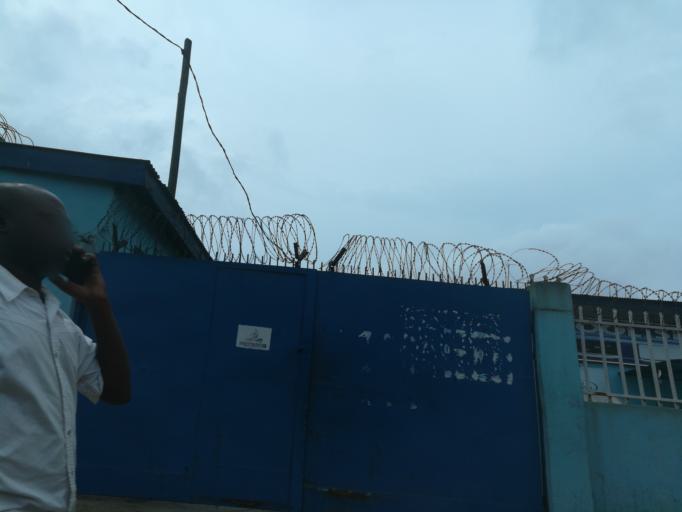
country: NG
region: Lagos
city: Oshodi
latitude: 6.5633
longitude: 3.3474
